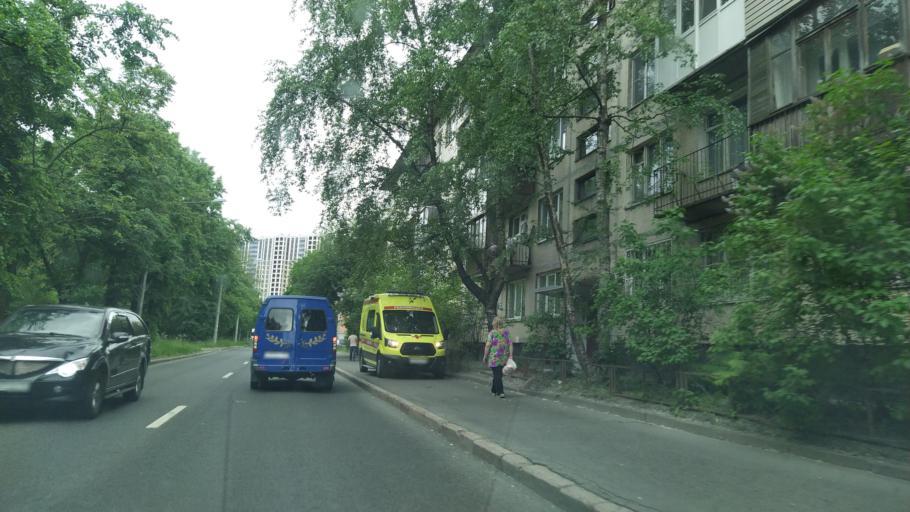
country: RU
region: St.-Petersburg
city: Avtovo
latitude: 59.8441
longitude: 30.3057
